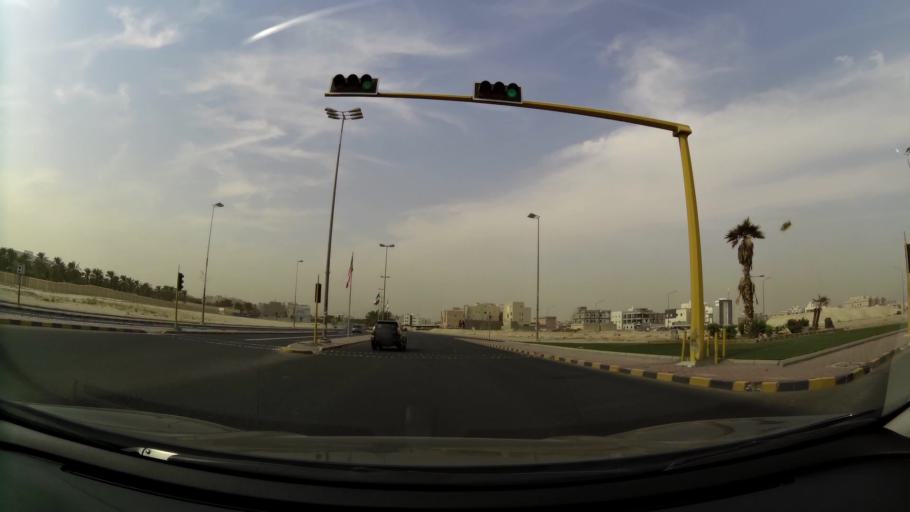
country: KW
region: Al Farwaniyah
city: Janub as Surrah
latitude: 29.2854
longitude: 48.0020
